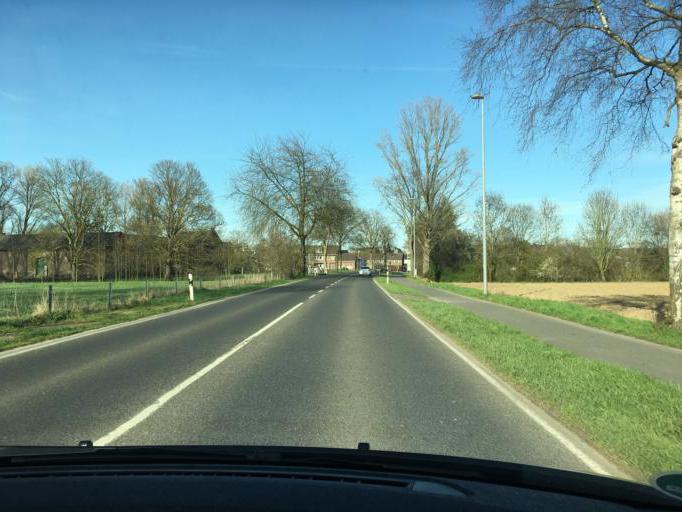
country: DE
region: North Rhine-Westphalia
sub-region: Regierungsbezirk Dusseldorf
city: Korschenbroich
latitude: 51.1876
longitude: 6.5602
